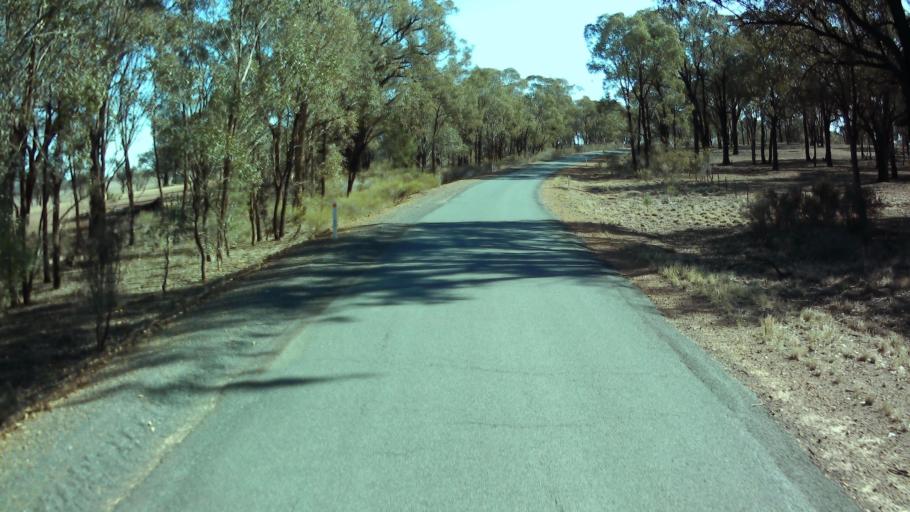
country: AU
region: New South Wales
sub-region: Weddin
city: Grenfell
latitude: -33.7850
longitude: 147.9586
